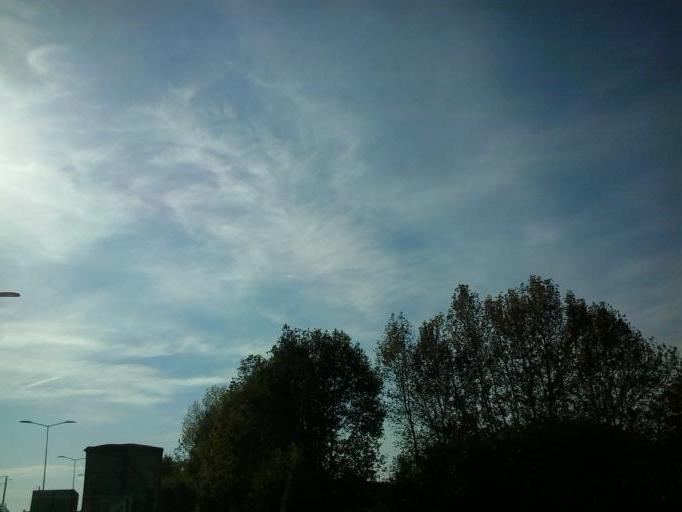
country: IT
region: Lombardy
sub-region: Provincia di Brescia
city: Roncadelle
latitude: 45.5399
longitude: 10.1823
